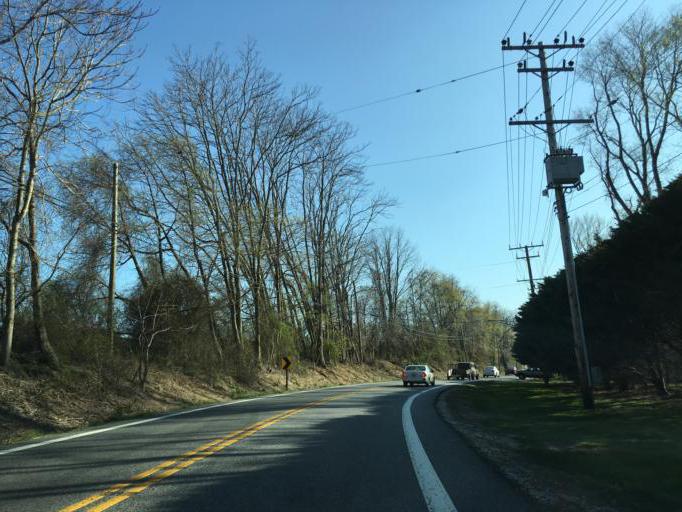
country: US
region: Maryland
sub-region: Baltimore County
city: Carney
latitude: 39.4127
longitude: -76.5108
